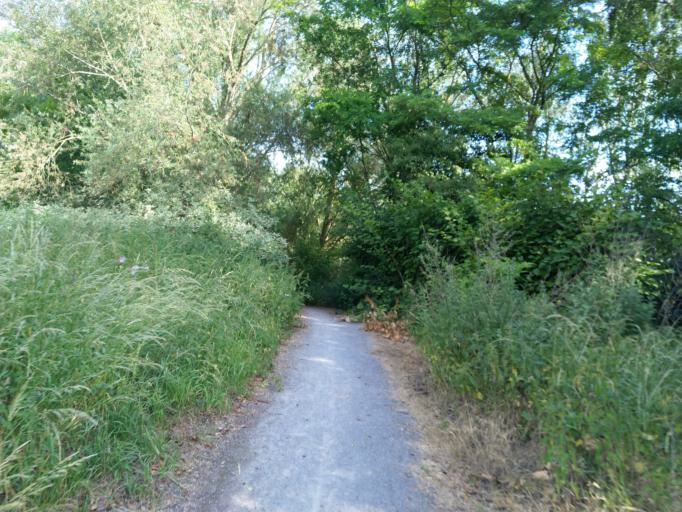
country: FR
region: Nord-Pas-de-Calais
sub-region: Departement du Nord
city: Rousies
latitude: 50.2827
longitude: 4.0168
